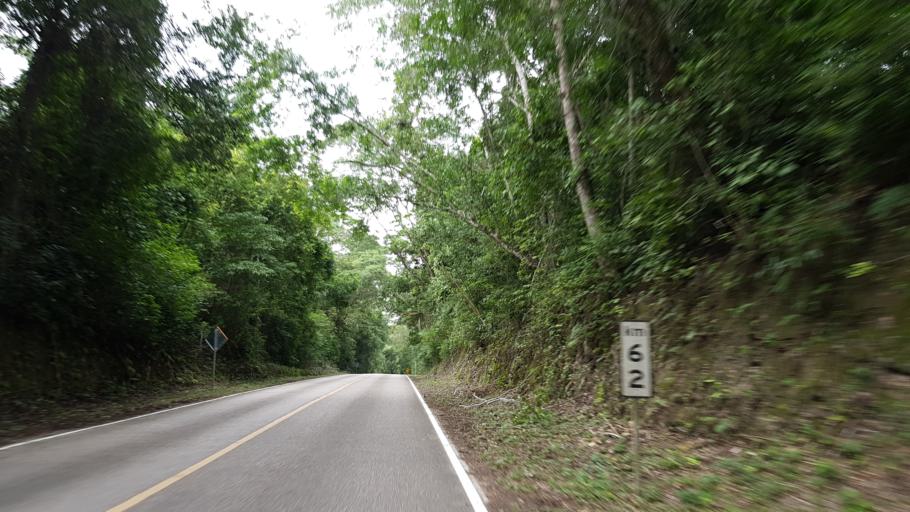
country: GT
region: Peten
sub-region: Municipio de San Jose
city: San Jose
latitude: 17.2156
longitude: -89.6118
